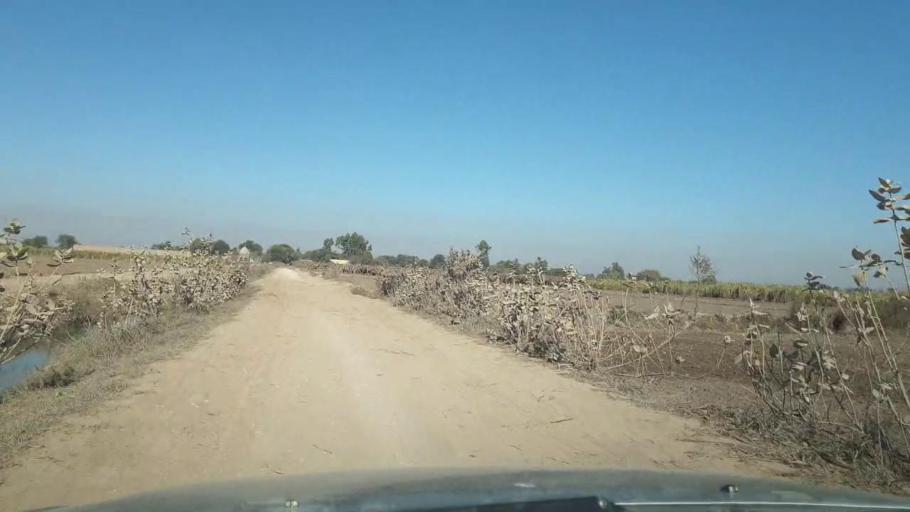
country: PK
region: Sindh
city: Ghotki
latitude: 28.0397
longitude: 69.2466
